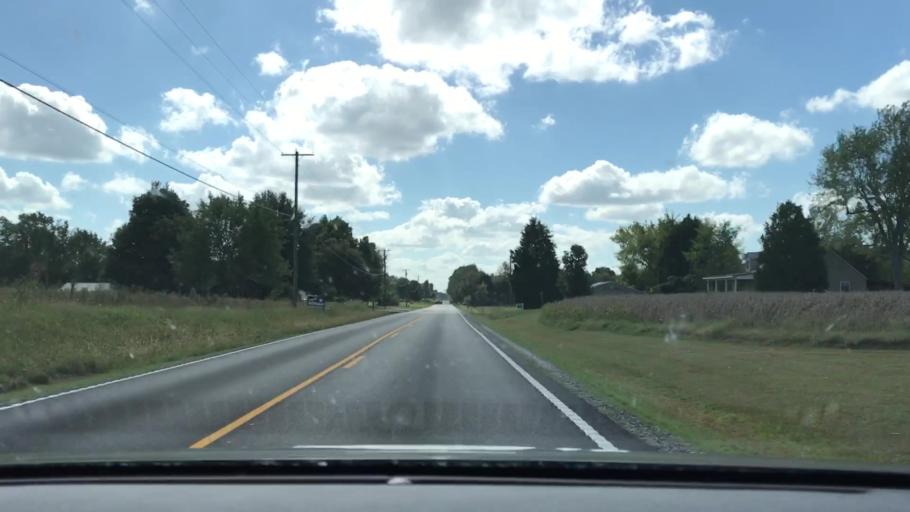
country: US
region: Kentucky
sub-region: Graves County
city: Mayfield
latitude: 36.8019
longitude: -88.5954
